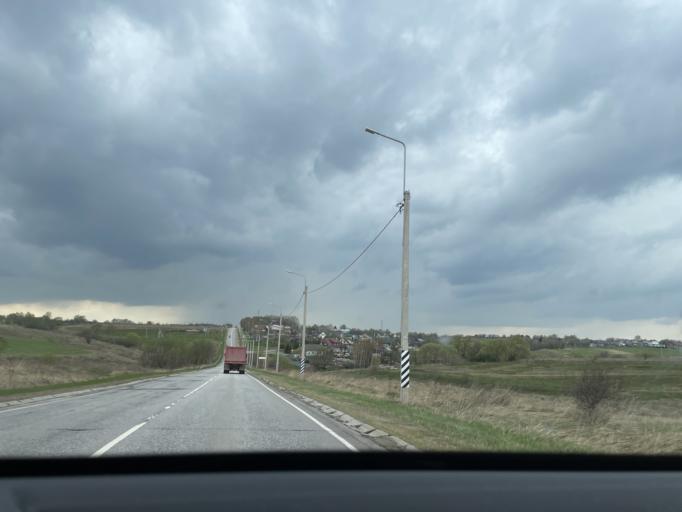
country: RU
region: Tula
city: Novogurovskiy
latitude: 54.5236
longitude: 37.4267
